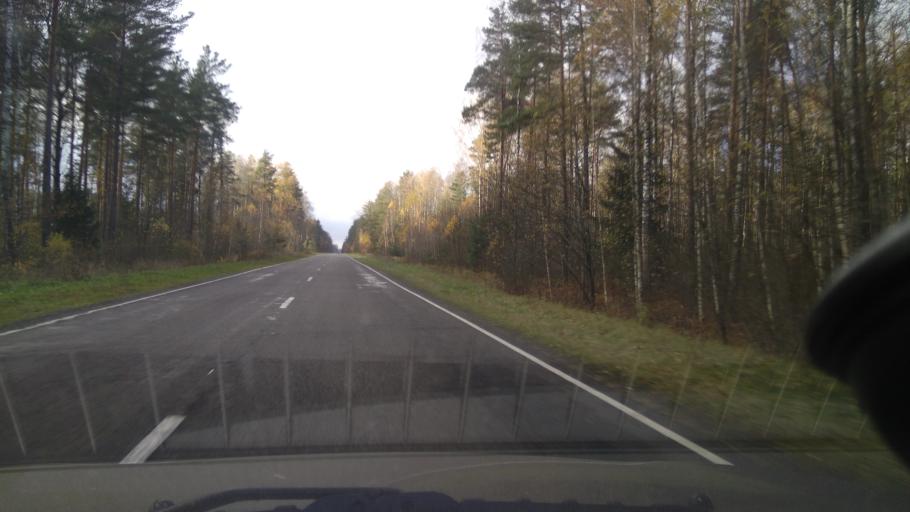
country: BY
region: Minsk
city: Urechcha
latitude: 53.2093
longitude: 27.9711
